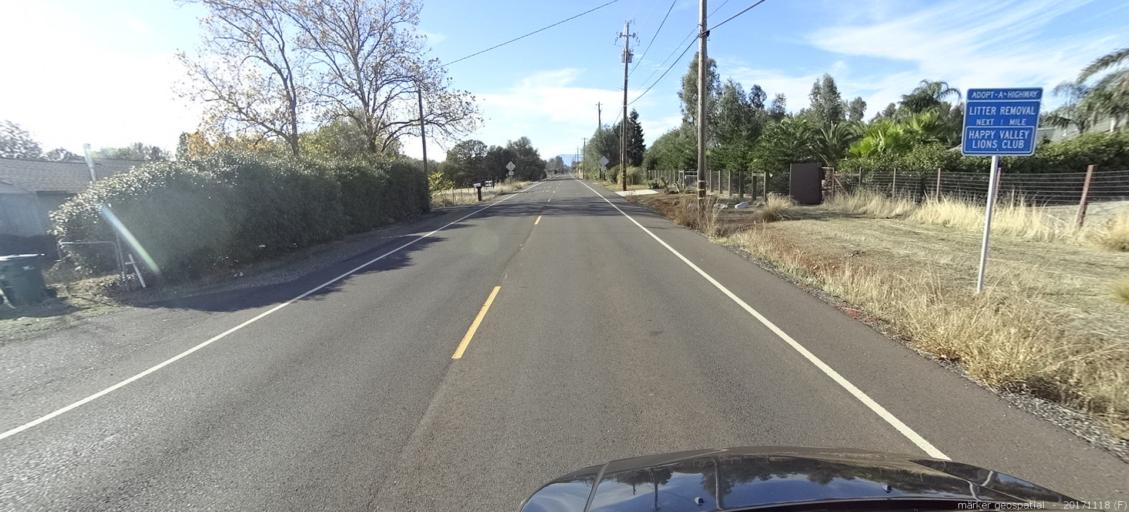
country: US
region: California
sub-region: Shasta County
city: Anderson
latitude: 40.4779
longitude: -122.3990
